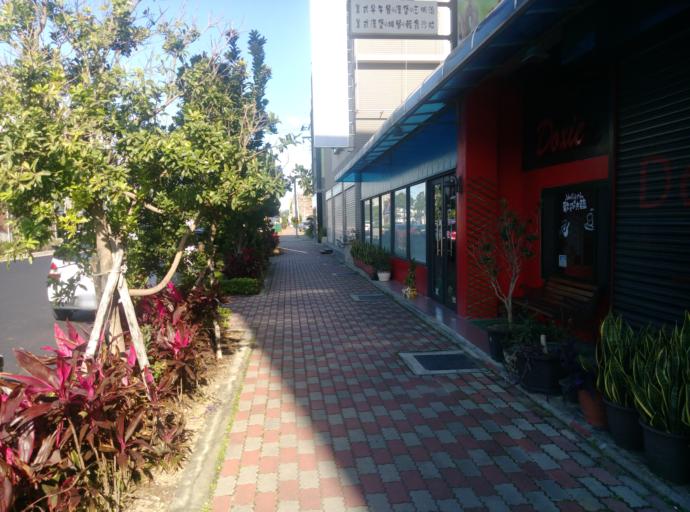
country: TW
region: Taiwan
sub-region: Hsinchu
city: Hsinchu
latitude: 24.6915
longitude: 120.9031
